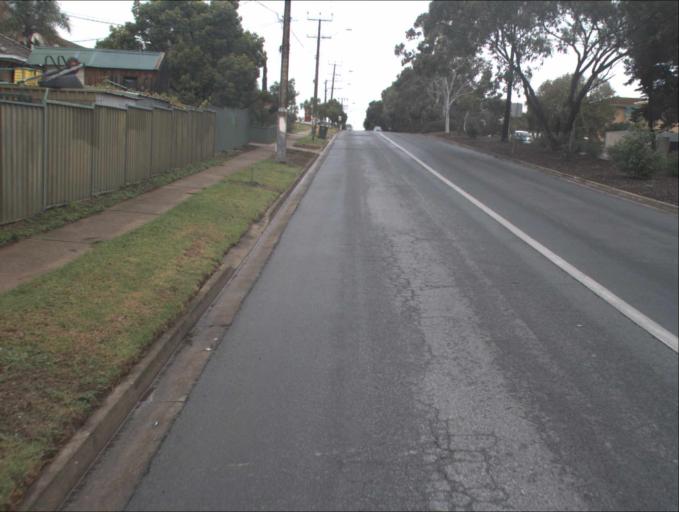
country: AU
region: South Australia
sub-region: Port Adelaide Enfield
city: Gilles Plains
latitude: -34.8394
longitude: 138.6627
